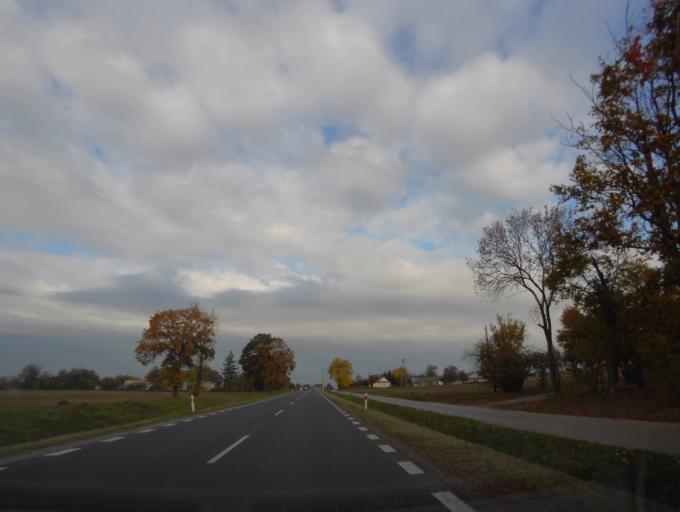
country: PL
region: Lublin Voivodeship
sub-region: Powiat lubelski
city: Wysokie
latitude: 50.8694
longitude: 22.6793
